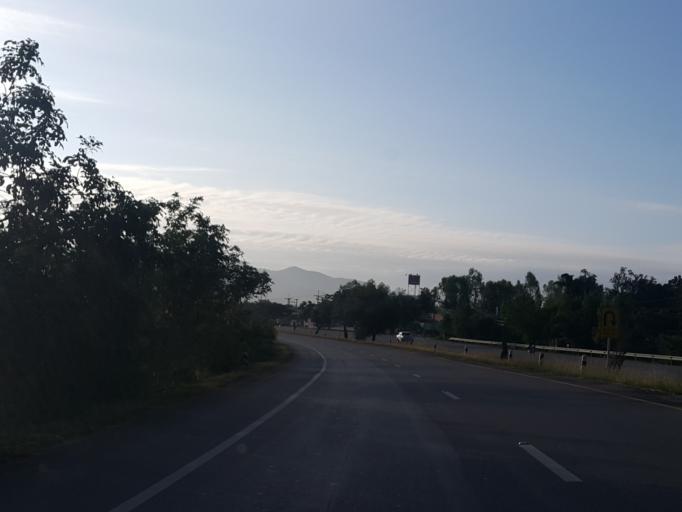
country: TH
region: Lampang
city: Lampang
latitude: 18.2752
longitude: 99.5219
